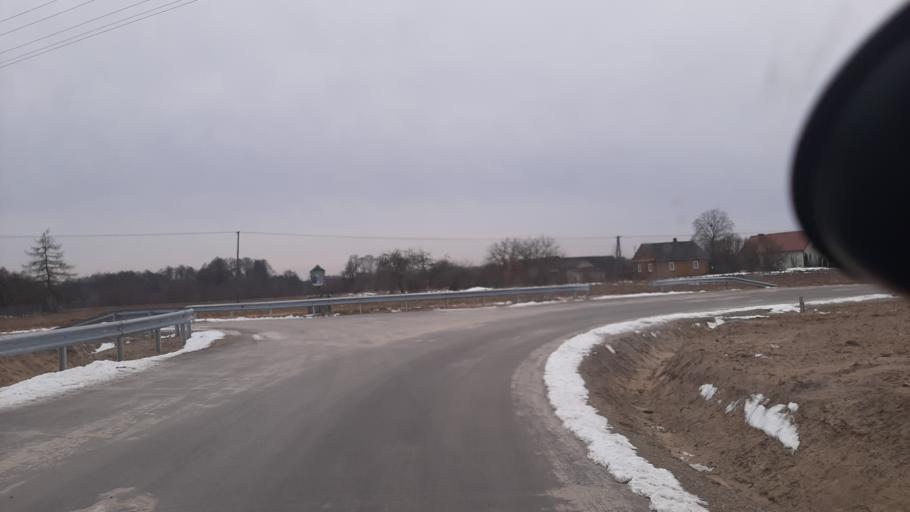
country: PL
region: Lublin Voivodeship
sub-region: Powiat lubartowski
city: Kamionka
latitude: 51.5126
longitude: 22.4713
